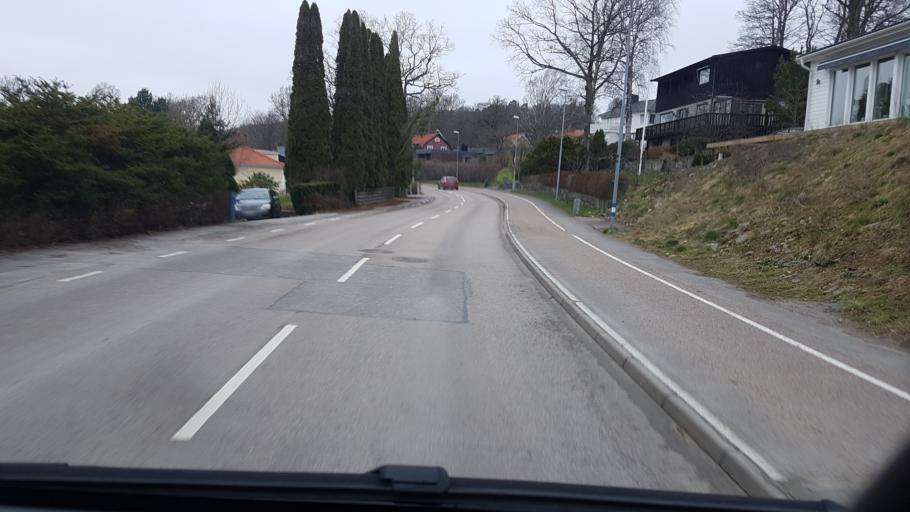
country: SE
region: Vaestra Goetaland
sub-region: Lerums Kommun
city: Lerum
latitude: 57.7724
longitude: 12.2471
